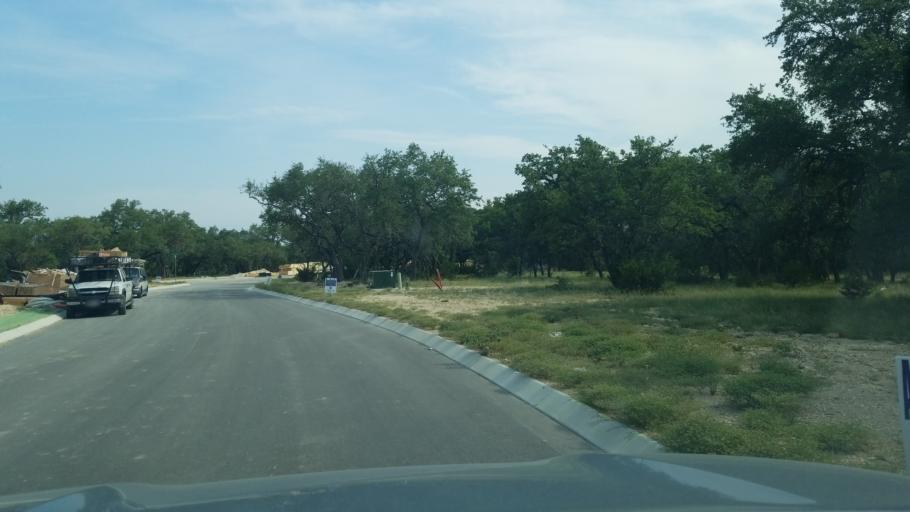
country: US
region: Texas
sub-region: Bexar County
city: Scenic Oaks
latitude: 29.7296
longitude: -98.6618
